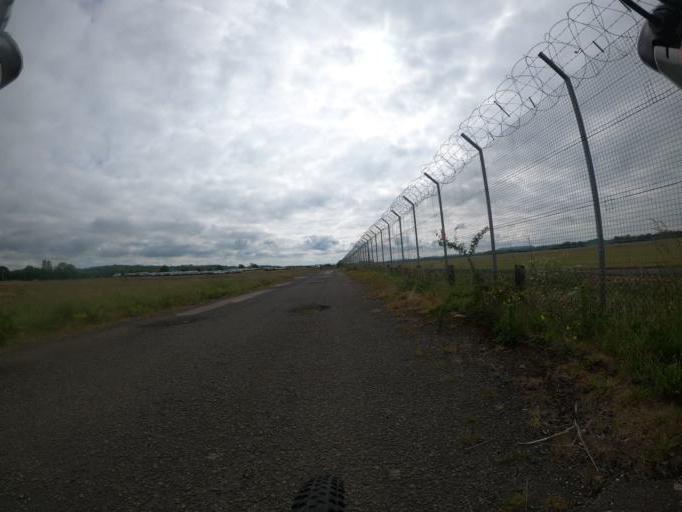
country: GB
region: Scotland
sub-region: Edinburgh
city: Ratho
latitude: 55.9454
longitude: -3.3778
